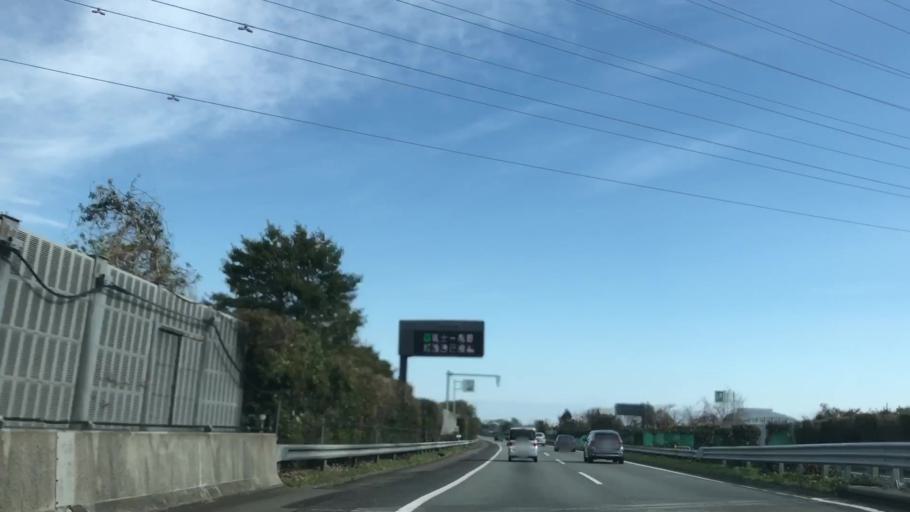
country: JP
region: Shizuoka
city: Hamamatsu
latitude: 34.7537
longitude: 137.7432
